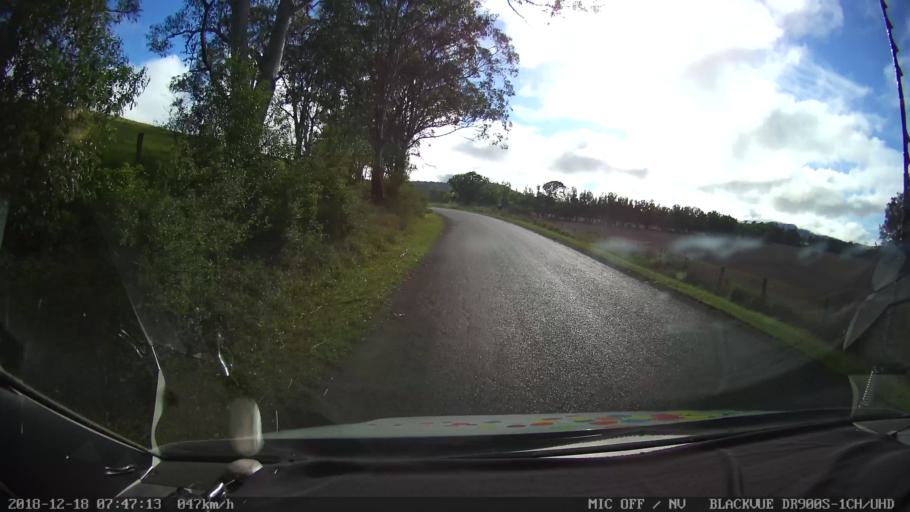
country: AU
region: New South Wales
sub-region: Kyogle
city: Kyogle
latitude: -28.4641
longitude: 152.5557
